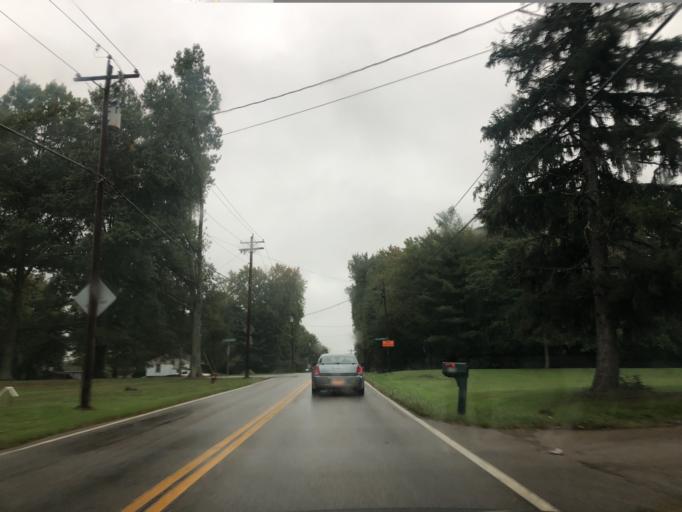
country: US
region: Ohio
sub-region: Clermont County
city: Mulberry
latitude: 39.2197
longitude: -84.2461
